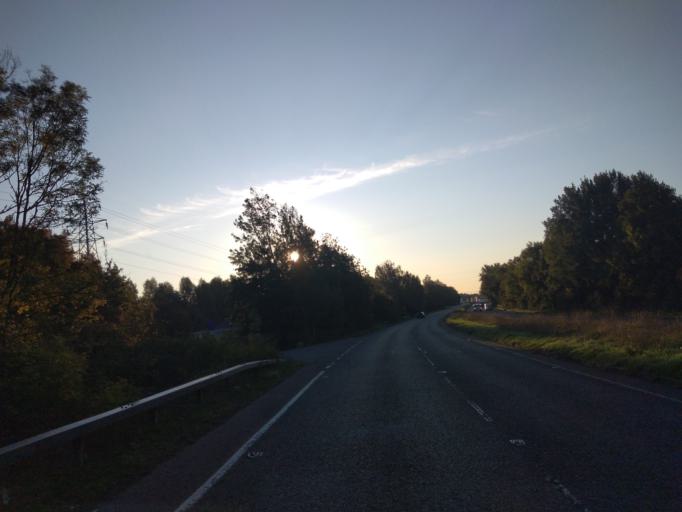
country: GB
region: England
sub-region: West Sussex
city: Rustington
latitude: 50.8234
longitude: -0.5119
